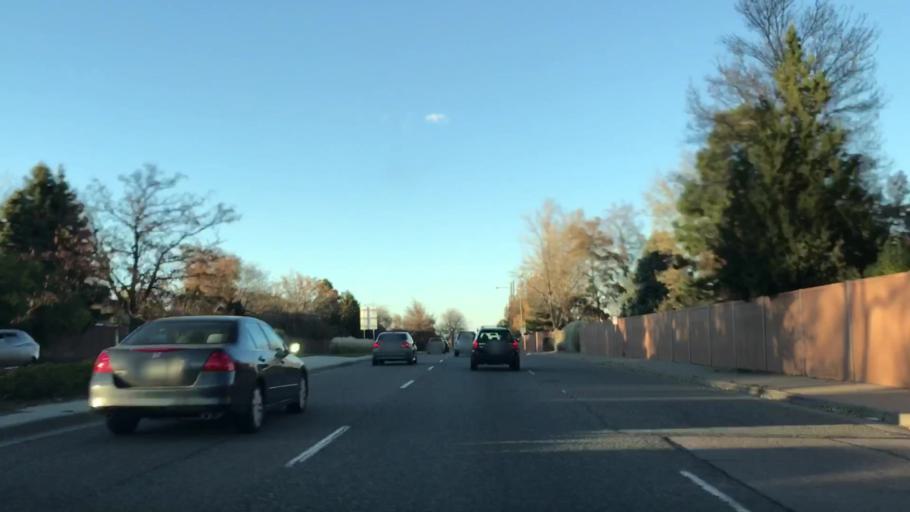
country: US
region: Colorado
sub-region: Arapahoe County
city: Castlewood
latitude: 39.6405
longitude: -104.8850
